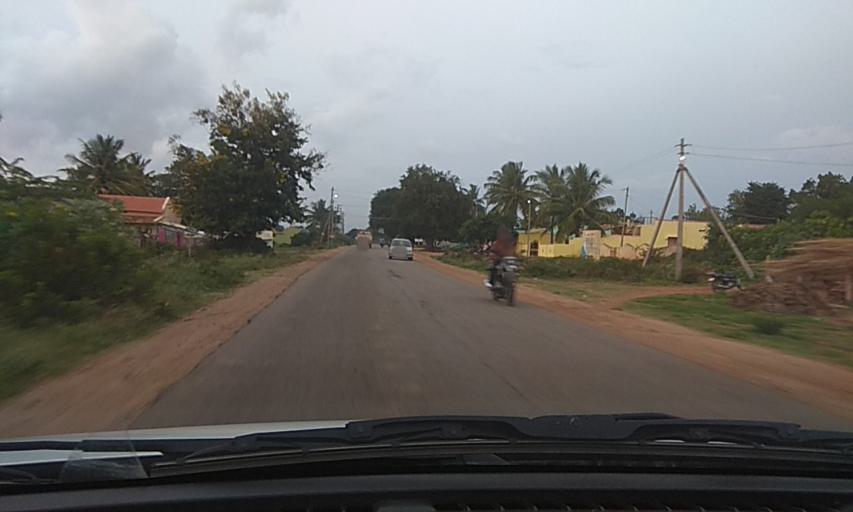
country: IN
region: Karnataka
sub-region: Chamrajnagar
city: Gundlupet
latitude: 11.8110
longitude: 76.7361
